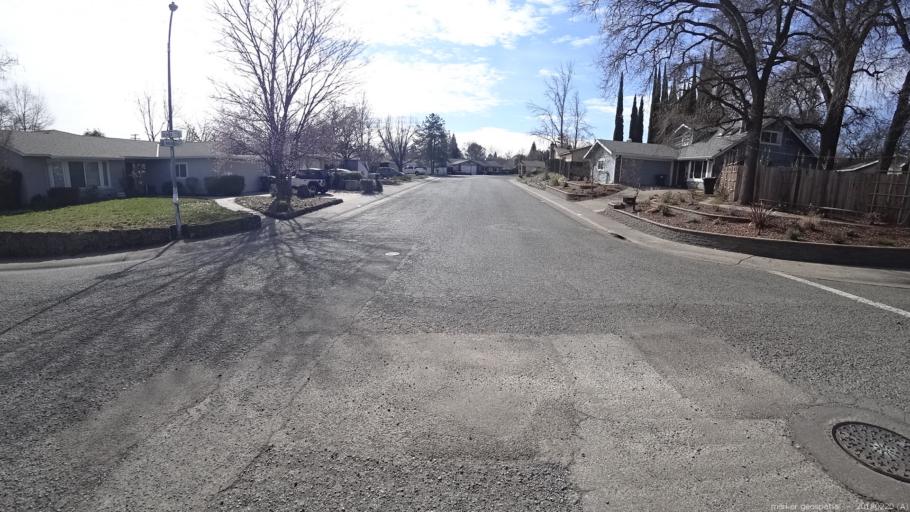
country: US
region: California
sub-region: Sacramento County
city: Orangevale
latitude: 38.6722
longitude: -121.2220
